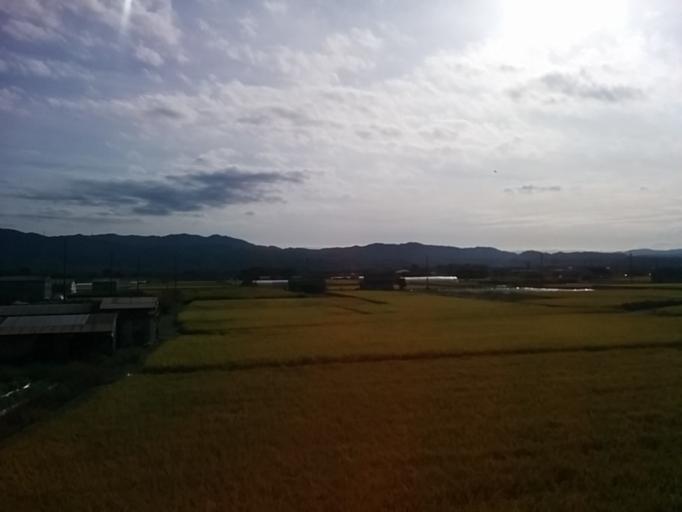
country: JP
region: Kyoto
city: Tanabe
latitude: 34.7871
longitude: 135.7883
